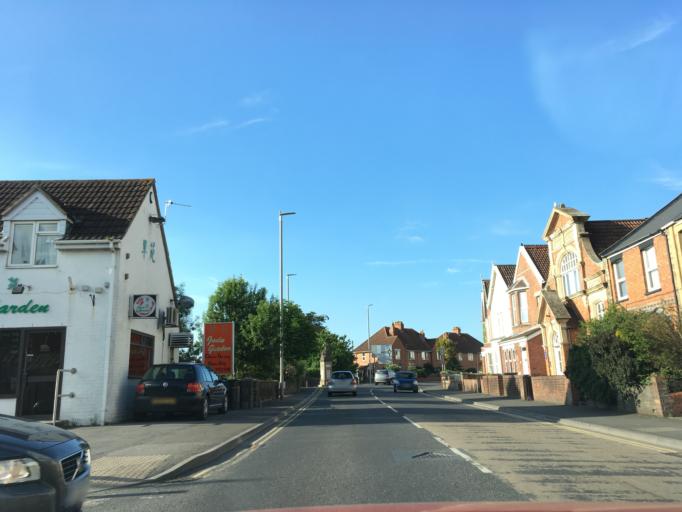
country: GB
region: England
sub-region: Somerset
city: Highbridge
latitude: 51.2228
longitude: -2.9747
